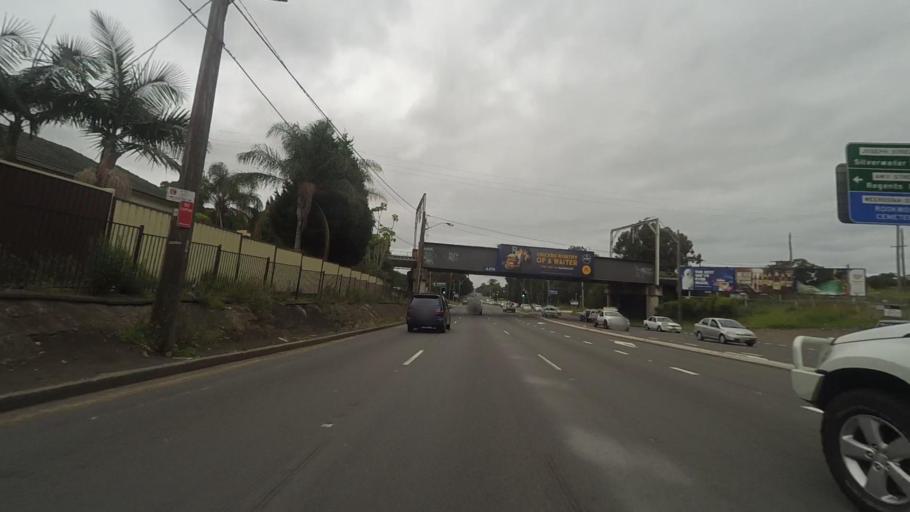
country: AU
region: New South Wales
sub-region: Auburn
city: Berala
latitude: -33.8855
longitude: 151.0398
